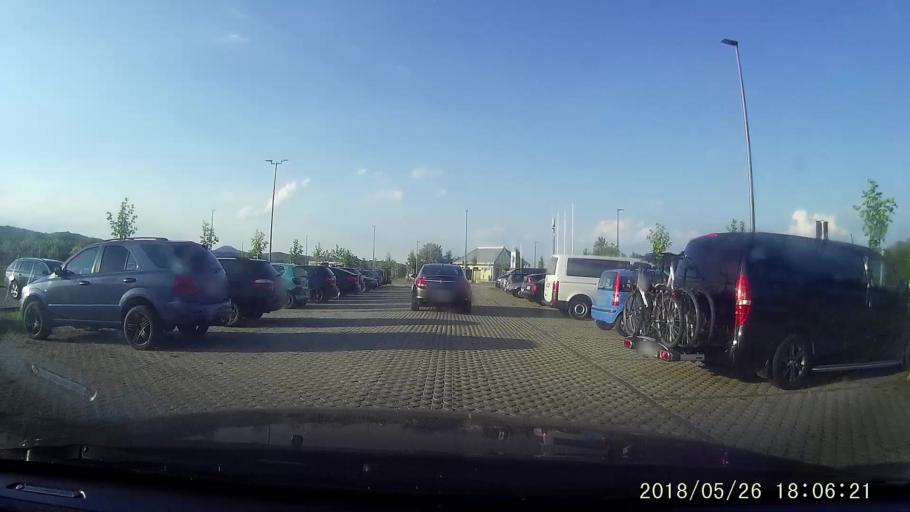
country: DE
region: Saxony
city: Schonau-Berzdorf
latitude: 51.0686
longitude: 14.9264
